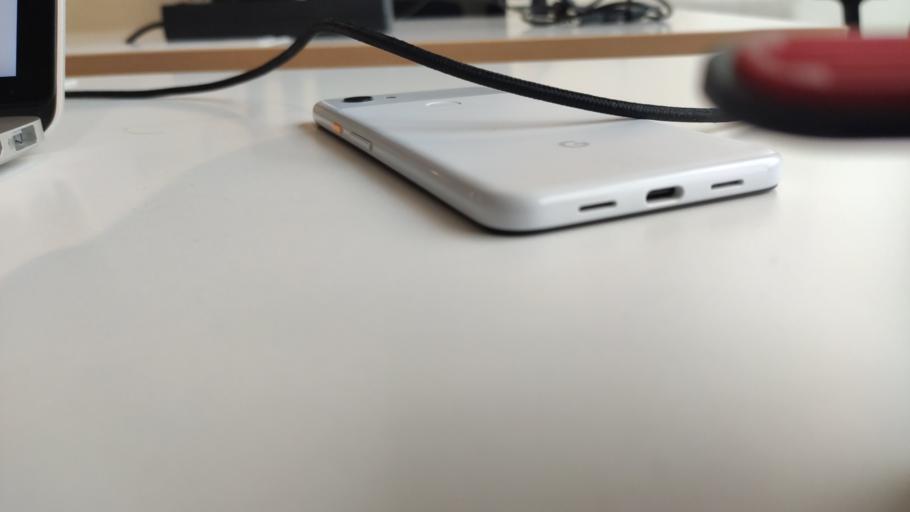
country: RU
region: Moskovskaya
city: Rogachevo
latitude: 56.4313
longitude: 37.1173
